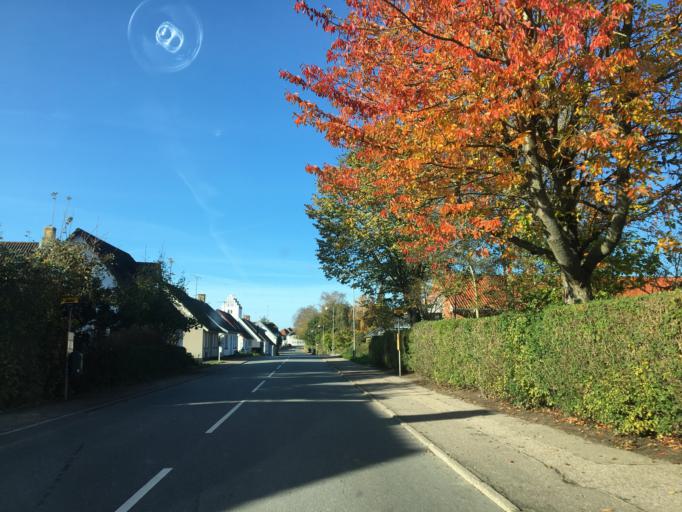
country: DK
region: Zealand
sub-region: Odsherred Kommune
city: Hojby
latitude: 55.8512
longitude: 11.5881
